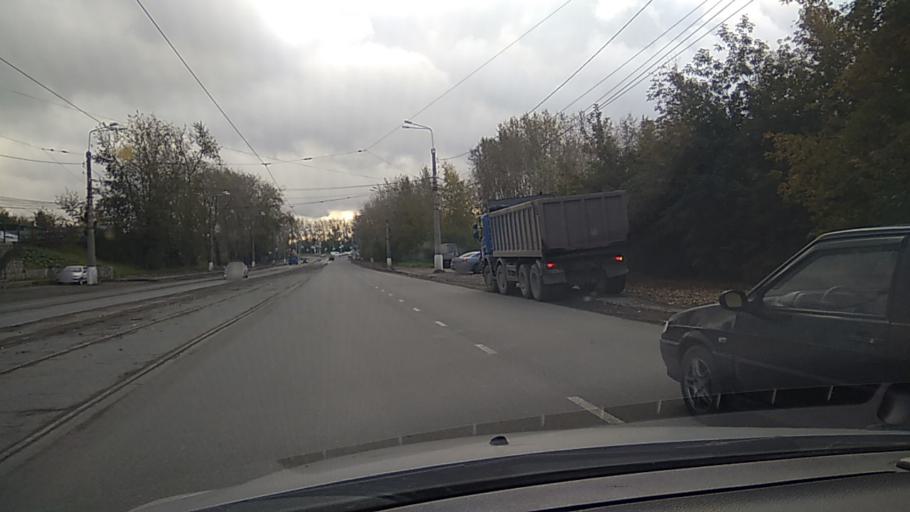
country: RU
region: Sverdlovsk
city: Nizhniy Tagil
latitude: 57.9247
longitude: 59.9905
